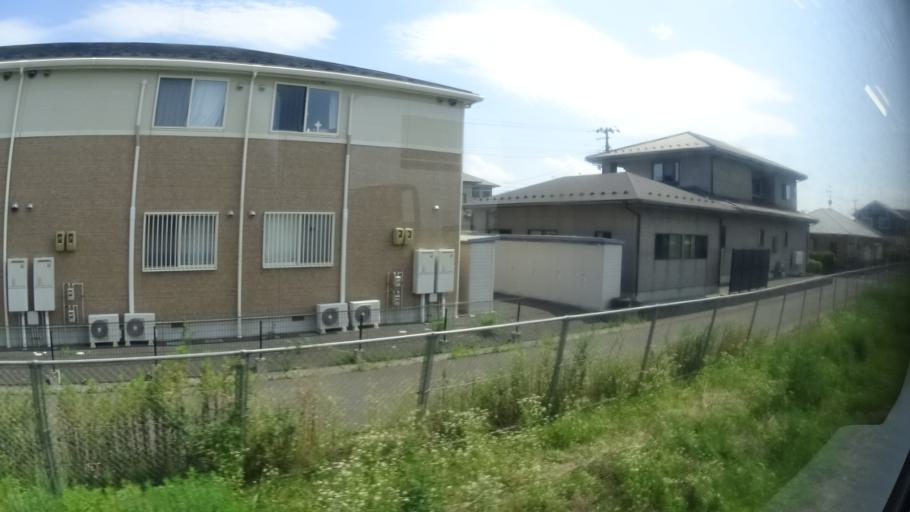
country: JP
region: Miyagi
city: Wakuya
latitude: 38.5801
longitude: 141.2381
